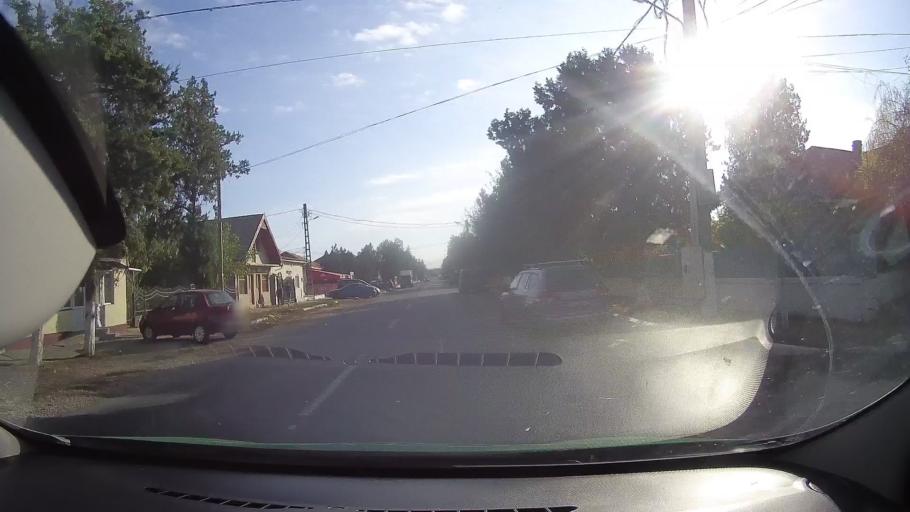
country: RO
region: Constanta
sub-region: Comuna Corbu
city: Corbu
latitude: 44.3837
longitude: 28.6623
